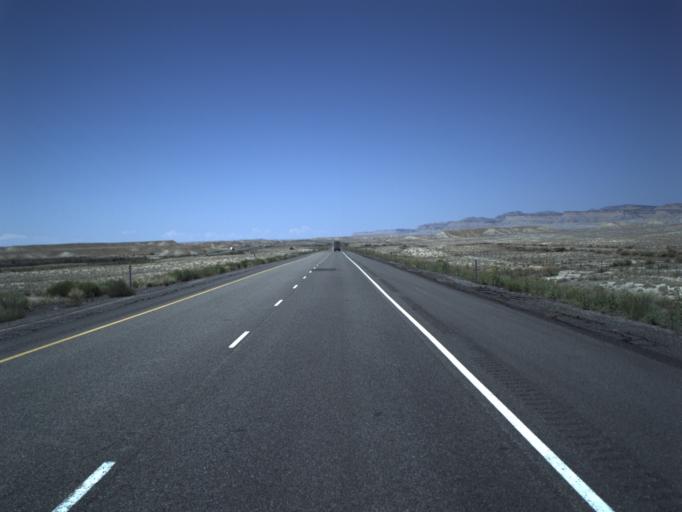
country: US
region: Utah
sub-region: Grand County
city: Moab
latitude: 38.9393
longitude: -109.4949
